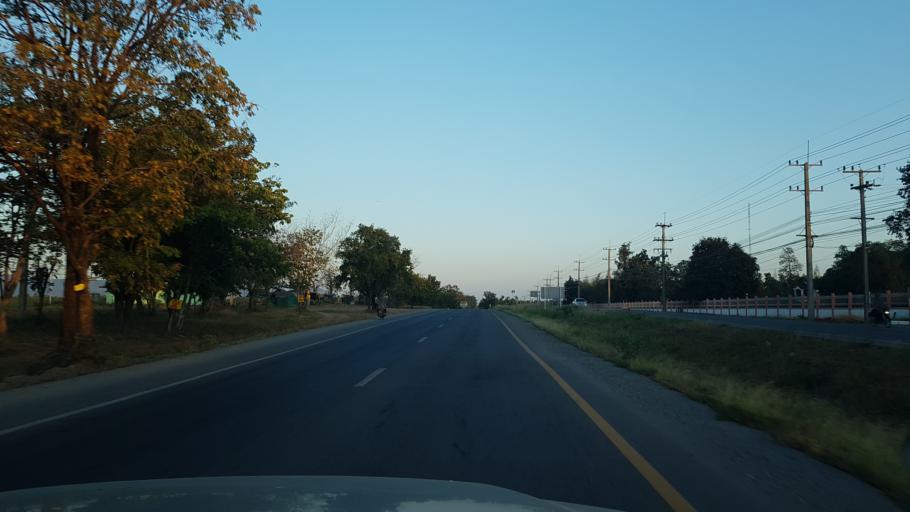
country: TH
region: Khon Kaen
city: Chum Phae
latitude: 16.5763
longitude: 102.0286
